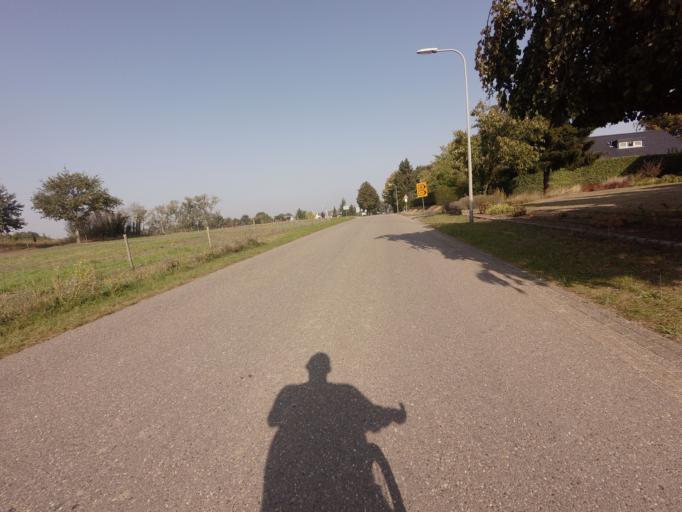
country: NL
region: Limburg
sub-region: Gemeente Beesel
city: Beesel
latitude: 51.2600
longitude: 5.9991
